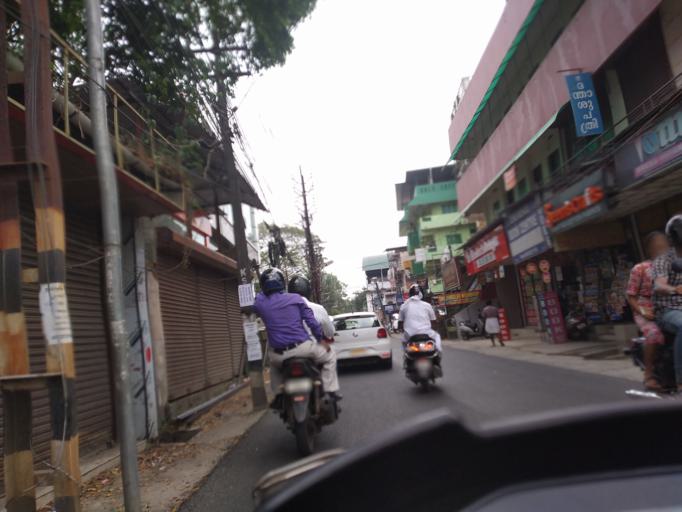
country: IN
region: Kerala
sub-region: Ernakulam
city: Cochin
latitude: 9.9409
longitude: 76.2957
